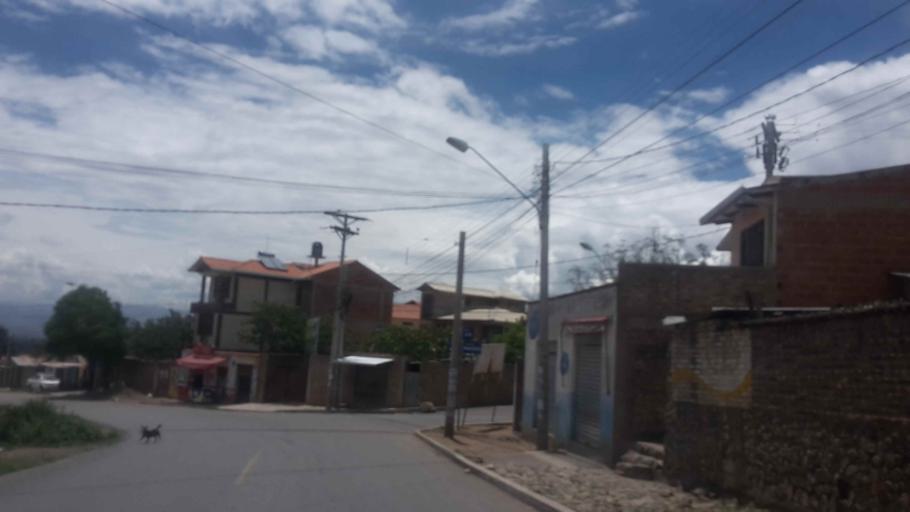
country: BO
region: Cochabamba
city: Cochabamba
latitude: -17.3476
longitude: -66.1805
